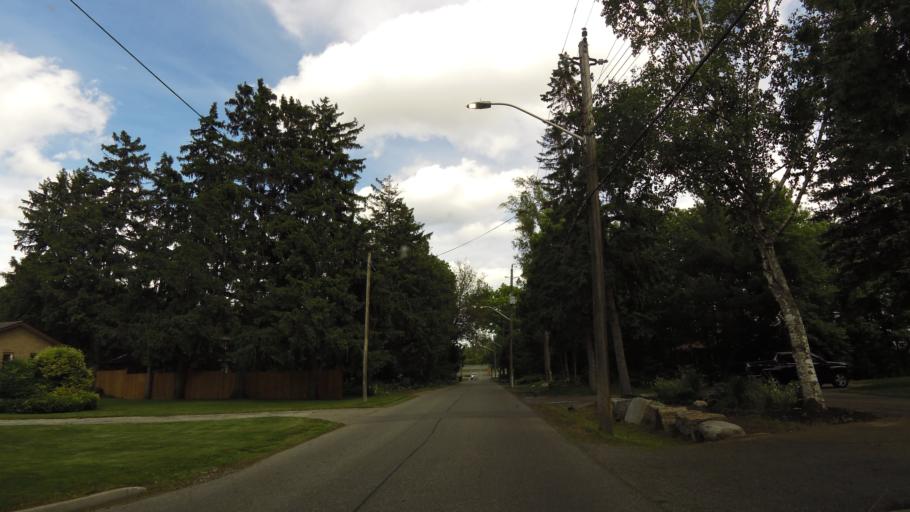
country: CA
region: Ontario
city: Mississauga
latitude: 43.5337
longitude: -79.6404
